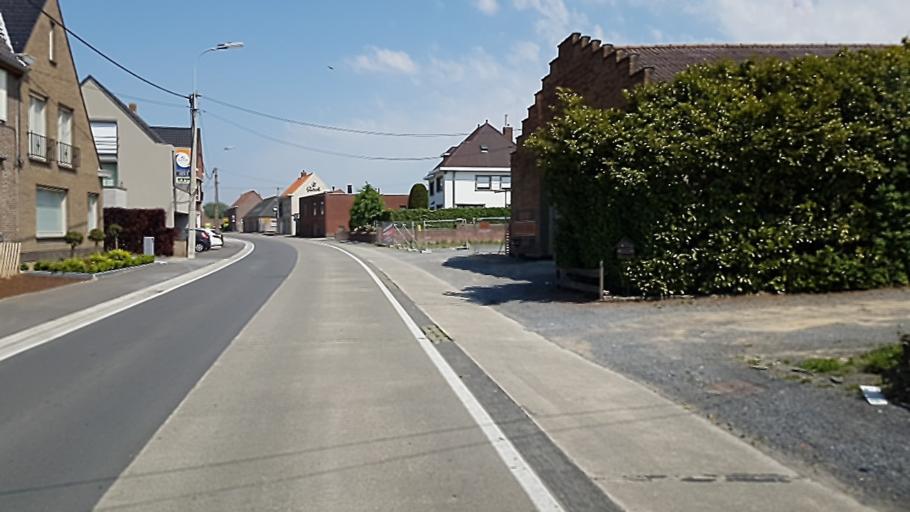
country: BE
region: Flanders
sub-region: Provincie West-Vlaanderen
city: Waregem
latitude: 50.8457
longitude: 3.4066
